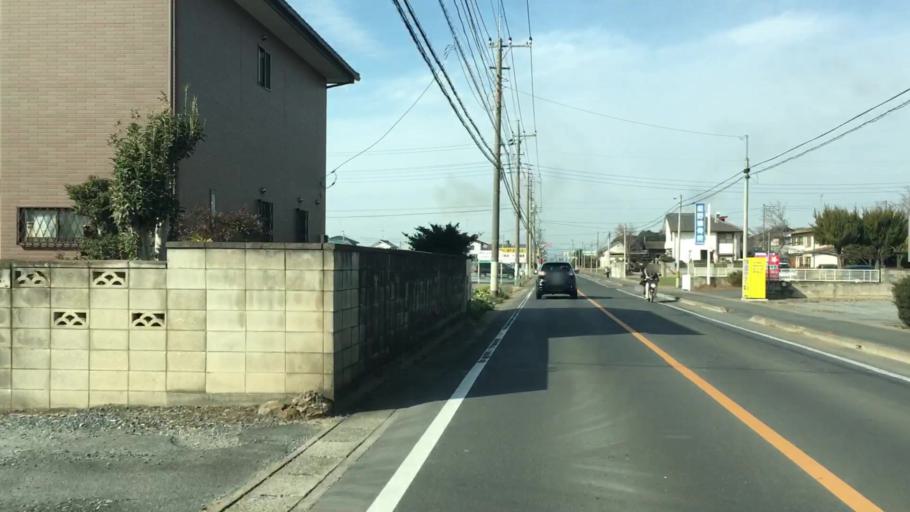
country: JP
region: Saitama
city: Menuma
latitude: 36.2400
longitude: 139.4559
